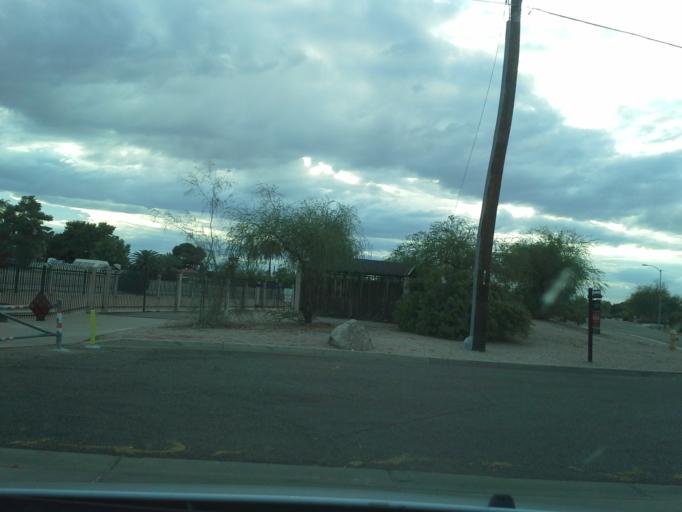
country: US
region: Arizona
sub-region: Maricopa County
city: Phoenix
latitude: 33.5439
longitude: -112.0518
